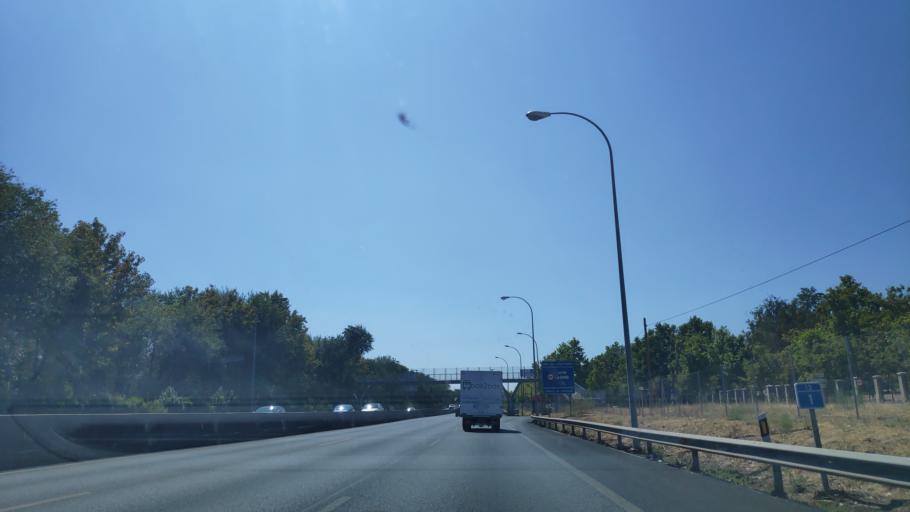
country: ES
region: Madrid
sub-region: Provincia de Madrid
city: Getafe
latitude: 40.3070
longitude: -3.7401
